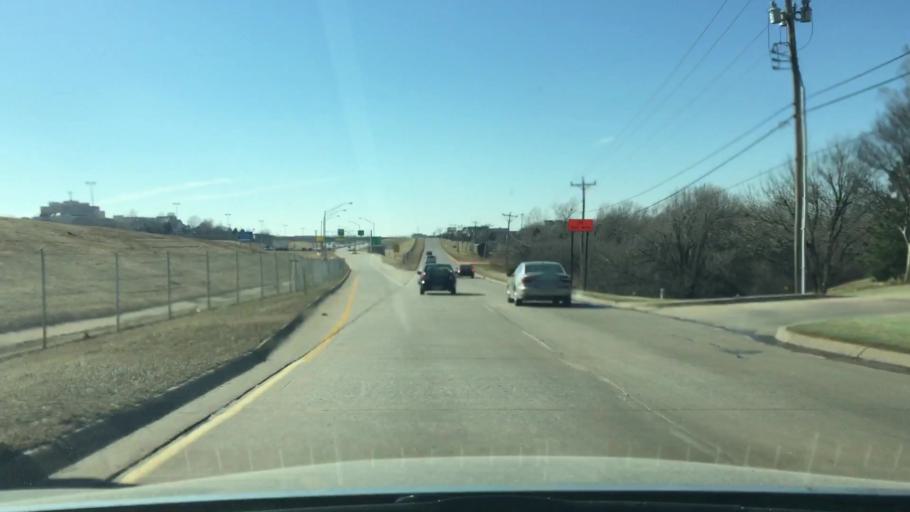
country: US
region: Oklahoma
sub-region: Oklahoma County
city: The Village
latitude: 35.6101
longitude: -97.5875
